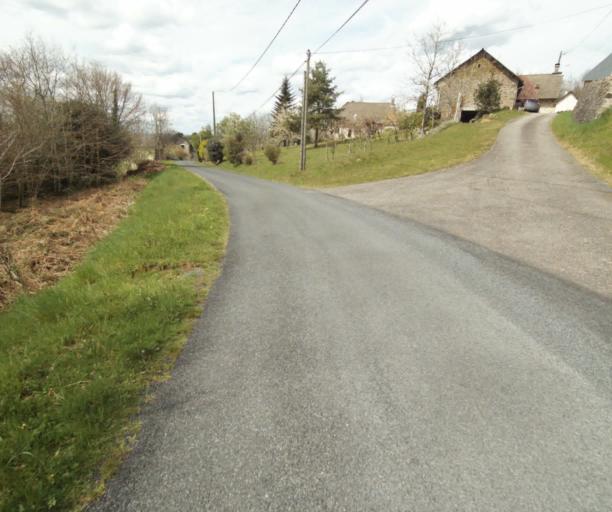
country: FR
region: Limousin
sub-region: Departement de la Correze
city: Laguenne
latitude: 45.2225
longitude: 1.8664
